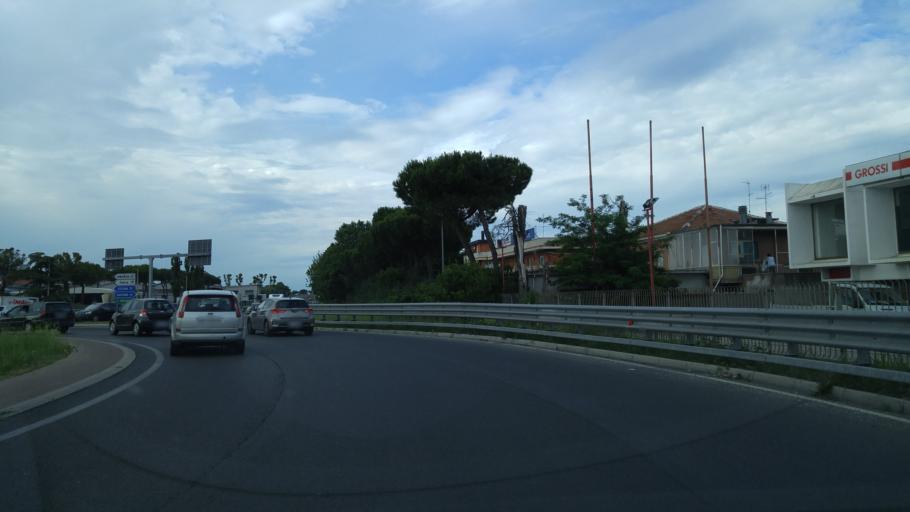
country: IT
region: Emilia-Romagna
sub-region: Provincia di Rimini
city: Rimini
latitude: 44.0639
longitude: 12.5417
